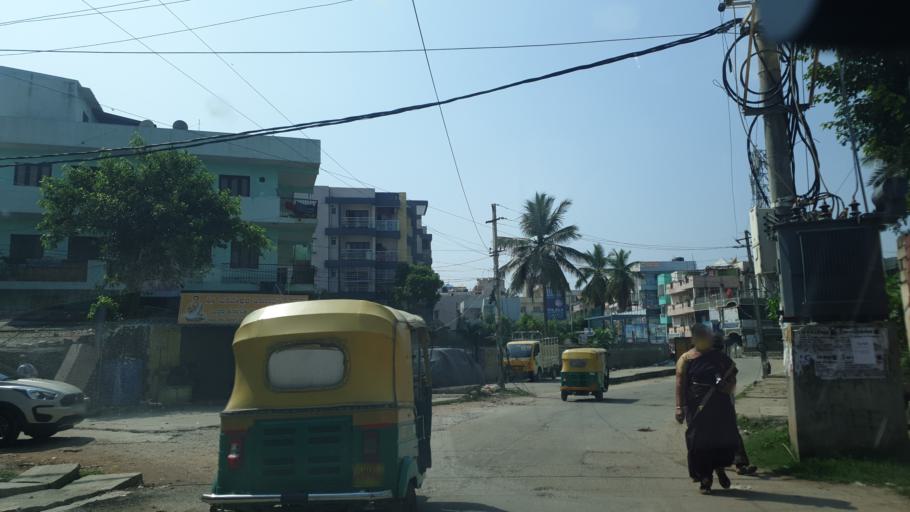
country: IN
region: Karnataka
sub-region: Bangalore Urban
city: Bangalore
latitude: 12.9781
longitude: 77.6664
